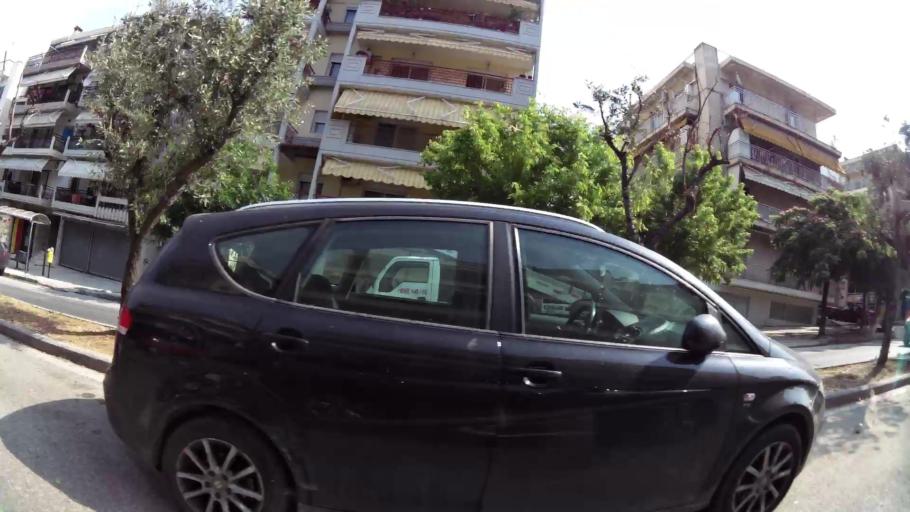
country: GR
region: Central Macedonia
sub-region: Nomos Thessalonikis
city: Sykies
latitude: 40.6510
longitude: 22.9543
